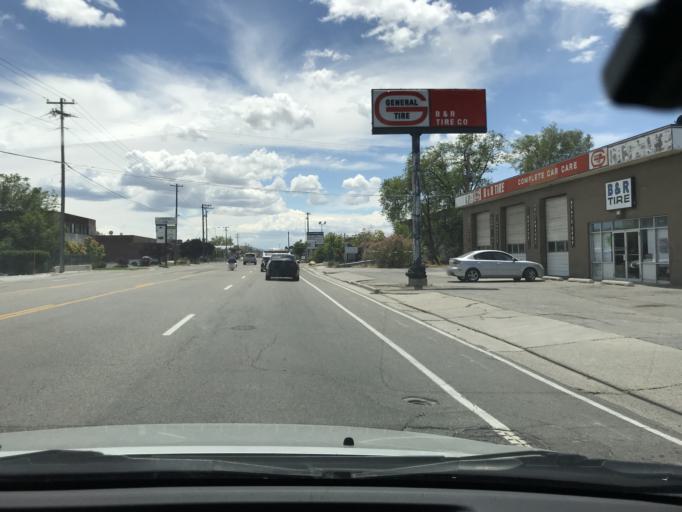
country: US
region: Utah
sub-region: Salt Lake County
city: Centerfield
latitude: 40.7068
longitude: -111.8998
